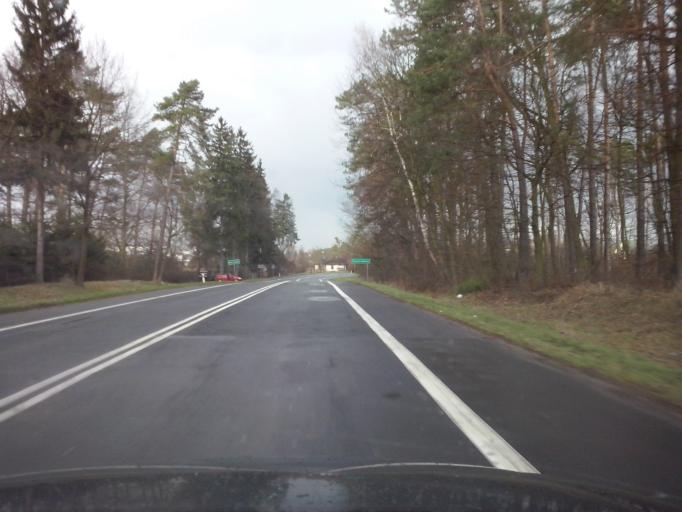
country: PL
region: Lublin Voivodeship
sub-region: Powiat krasnostawski
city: Krasnystaw
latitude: 51.0099
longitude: 23.1898
